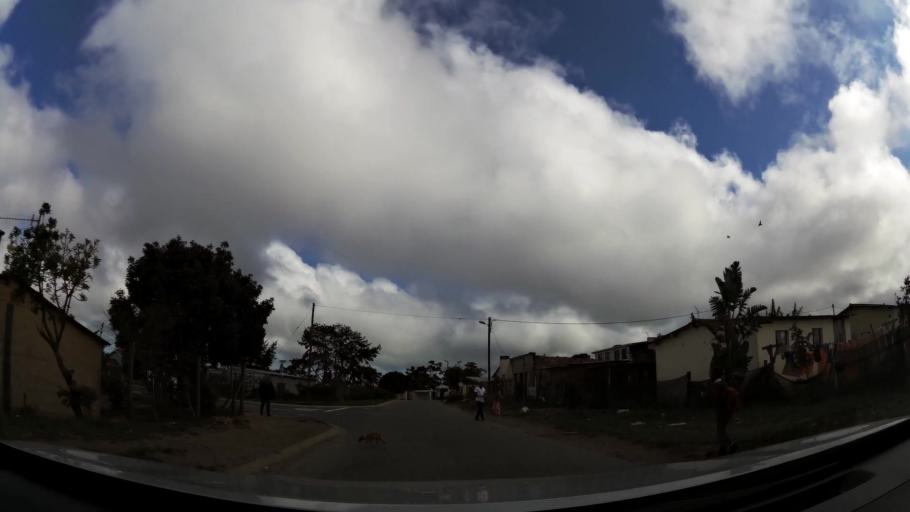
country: ZA
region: Western Cape
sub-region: Eden District Municipality
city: Plettenberg Bay
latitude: -34.0513
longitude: 23.3398
